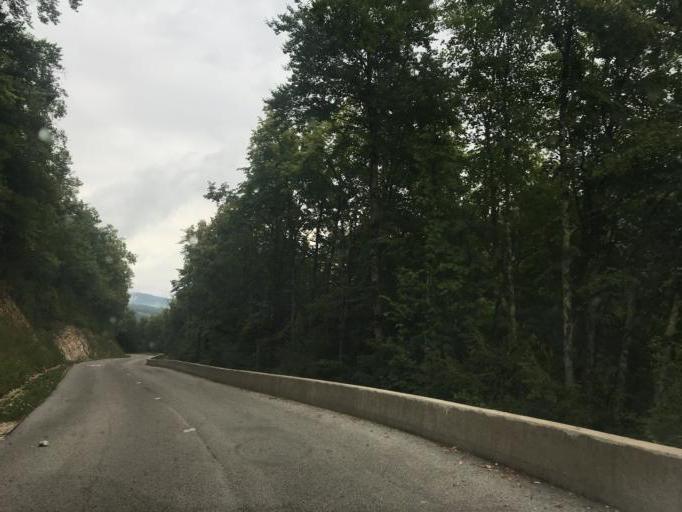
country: FR
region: Franche-Comte
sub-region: Departement du Jura
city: Lavans-les-Saint-Claude
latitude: 46.3395
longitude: 5.7678
